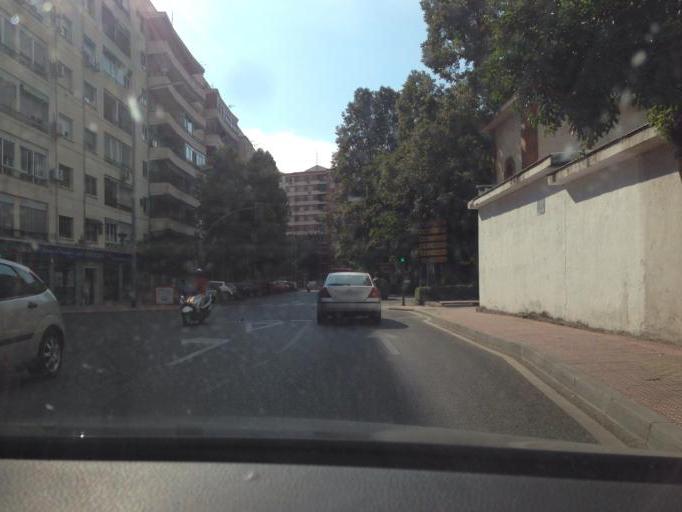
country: ES
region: Madrid
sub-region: Provincia de Madrid
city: Alcala de Henares
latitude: 40.4853
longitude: -3.3702
